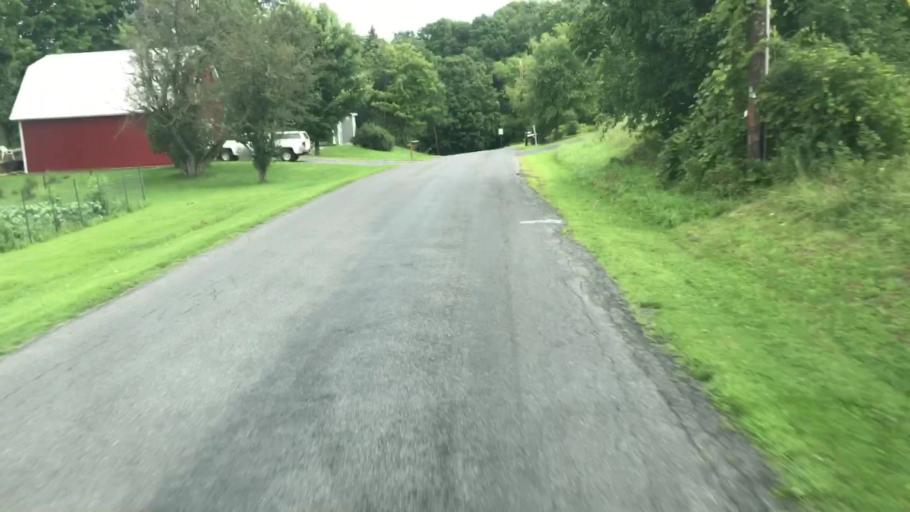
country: US
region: New York
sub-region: Onondaga County
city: Skaneateles
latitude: 42.9813
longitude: -76.4517
